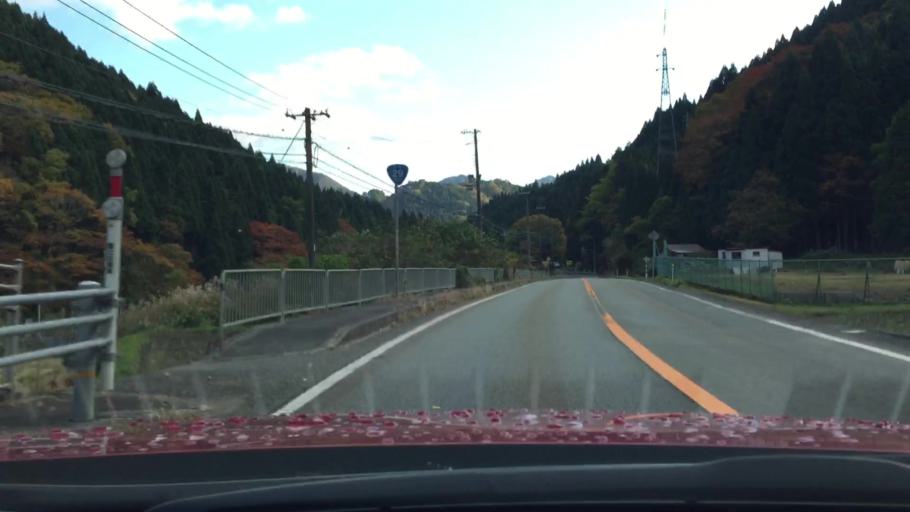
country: JP
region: Hyogo
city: Yamazakicho-nakabirose
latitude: 35.1846
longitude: 134.5342
